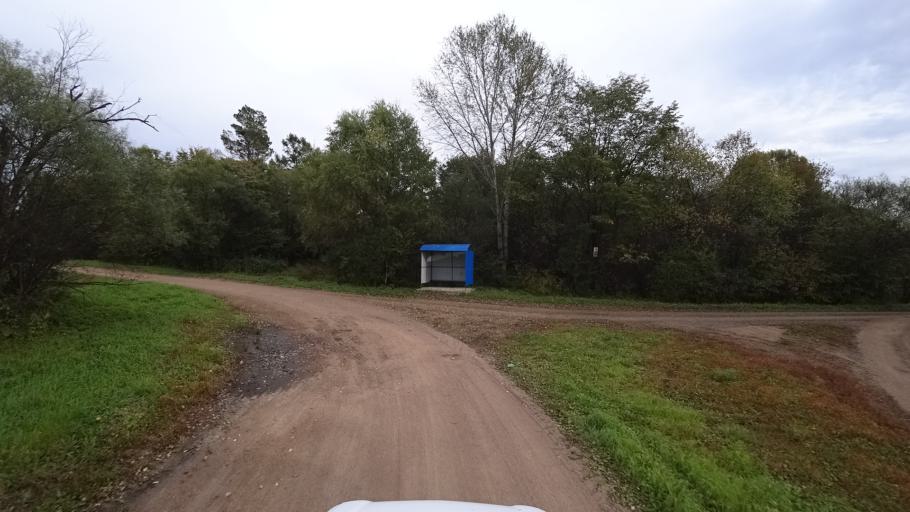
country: RU
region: Amur
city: Arkhara
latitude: 49.4349
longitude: 130.2657
